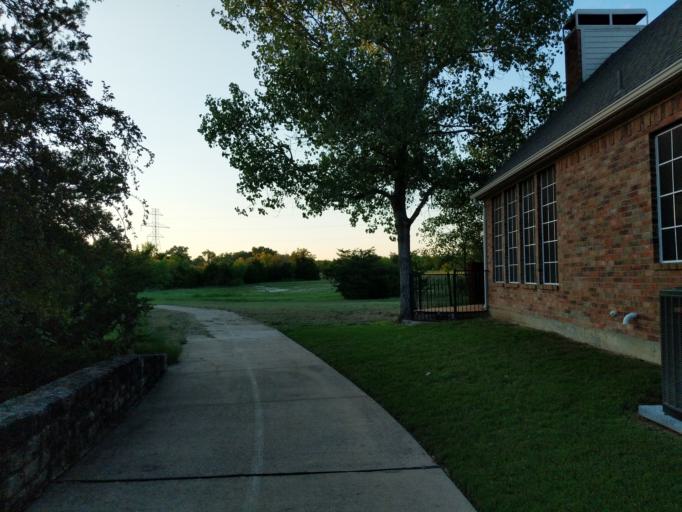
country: US
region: Texas
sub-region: Collin County
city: Murphy
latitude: 33.0030
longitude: -96.6566
